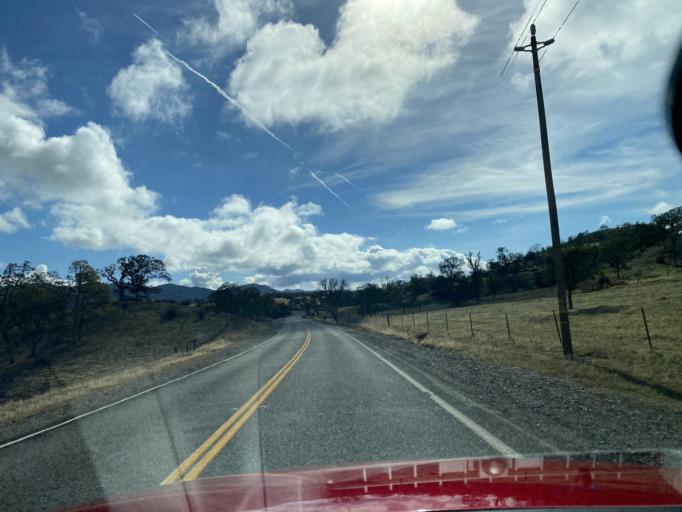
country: US
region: California
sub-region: Glenn County
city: Willows
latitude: 39.4858
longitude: -122.5182
